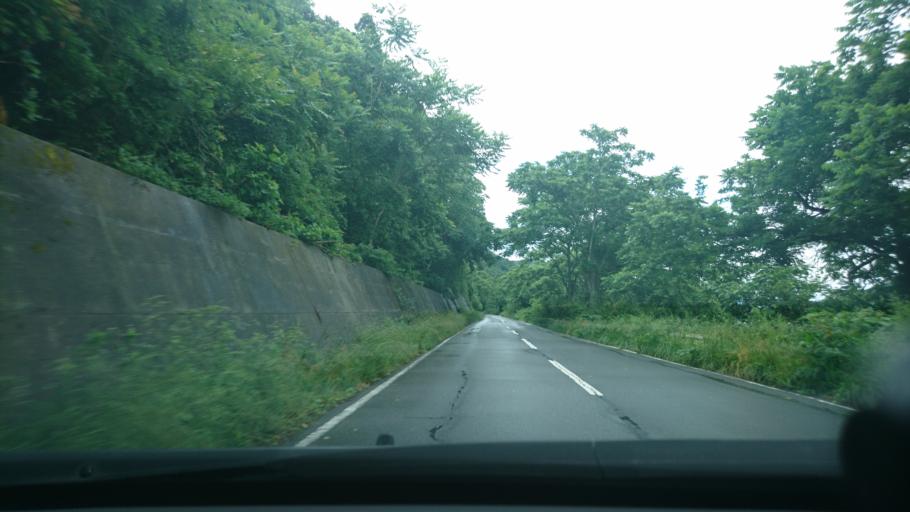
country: JP
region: Miyagi
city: Wakuya
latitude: 38.6670
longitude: 141.2837
